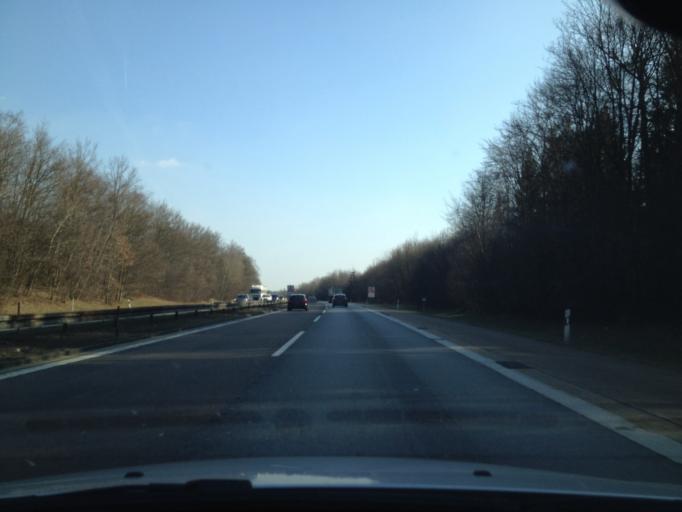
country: DE
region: Bavaria
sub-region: Regierungsbezirk Unterfranken
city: Esselbach
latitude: 49.8460
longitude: 9.5039
